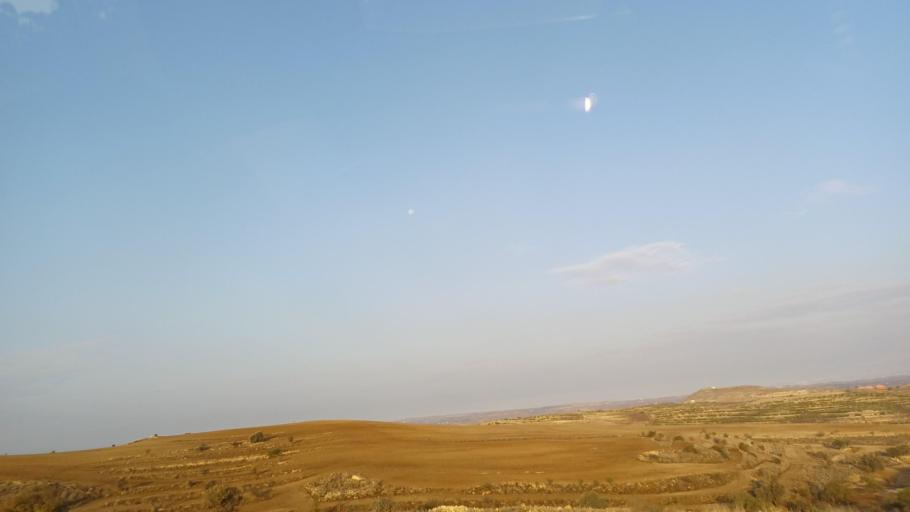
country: CY
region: Larnaka
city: Athienou
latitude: 35.0209
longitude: 33.5443
